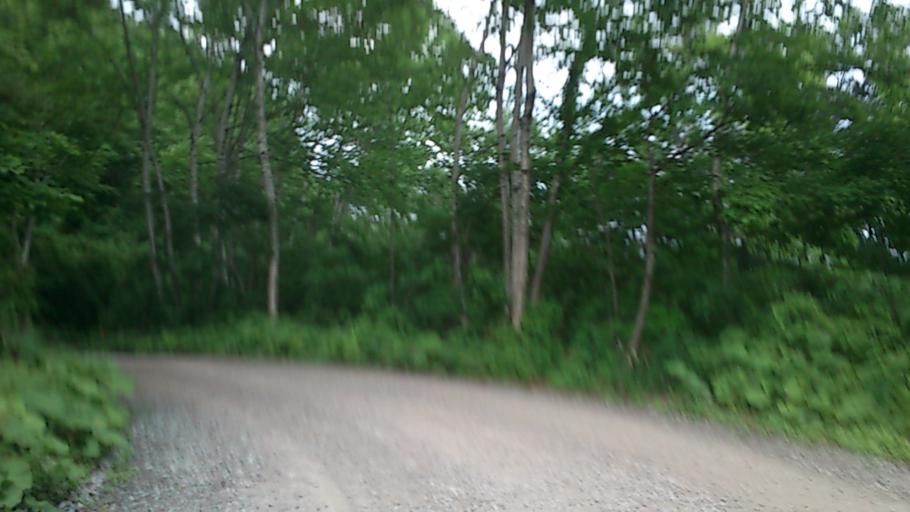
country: JP
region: Aomori
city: Hirosaki
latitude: 40.5585
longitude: 140.1664
